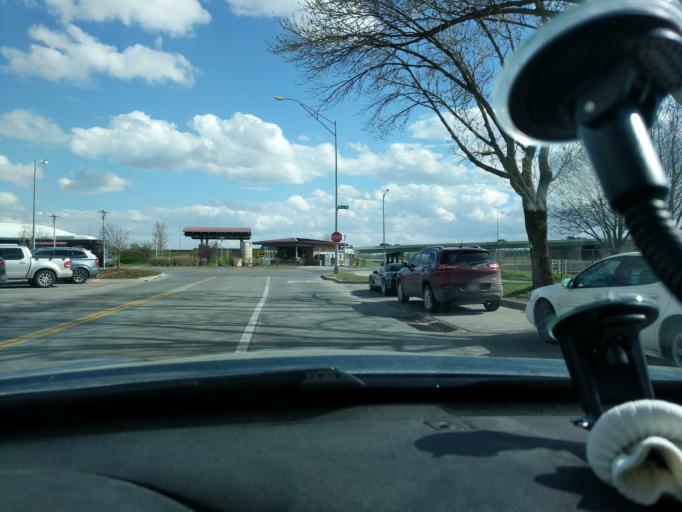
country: US
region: Nebraska
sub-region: Douglas County
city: Ralston
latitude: 41.2387
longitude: -96.0166
